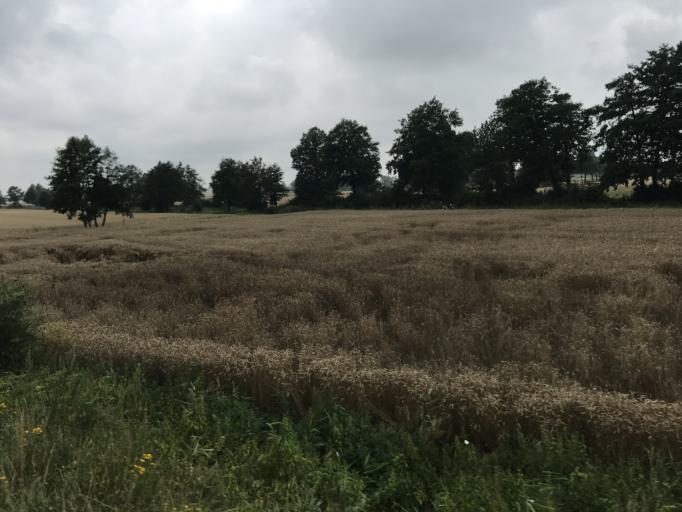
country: PL
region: Warmian-Masurian Voivodeship
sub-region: Powiat elblaski
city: Gronowo Elblaskie
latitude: 54.0965
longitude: 19.3212
